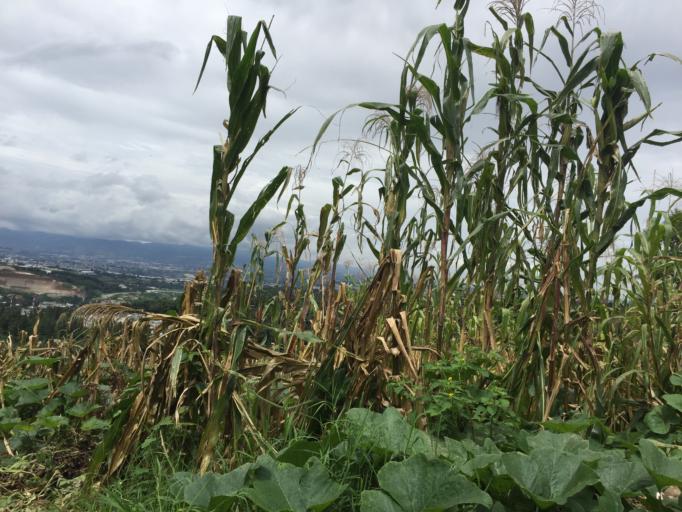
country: GT
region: Guatemala
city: Villa Canales
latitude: 14.4790
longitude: -90.5250
